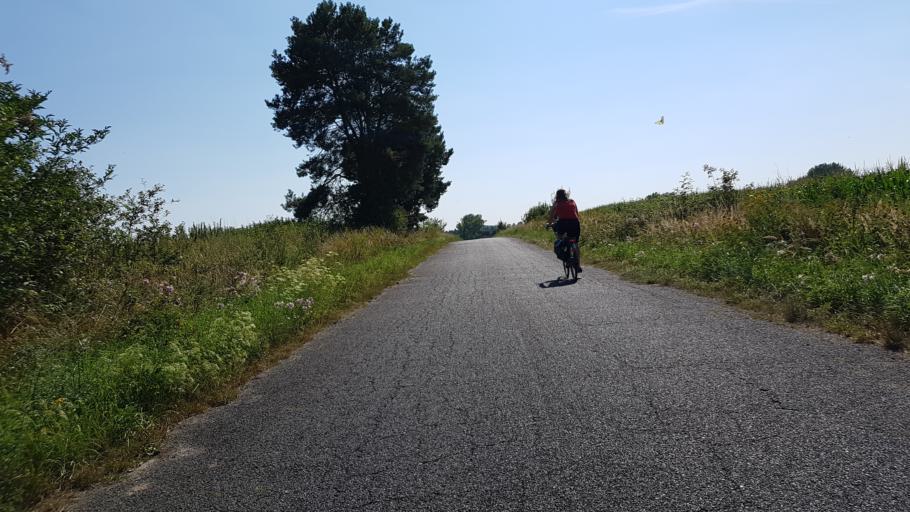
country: PL
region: West Pomeranian Voivodeship
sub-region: Powiat gryfinski
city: Gryfino
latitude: 53.1522
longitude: 14.5170
